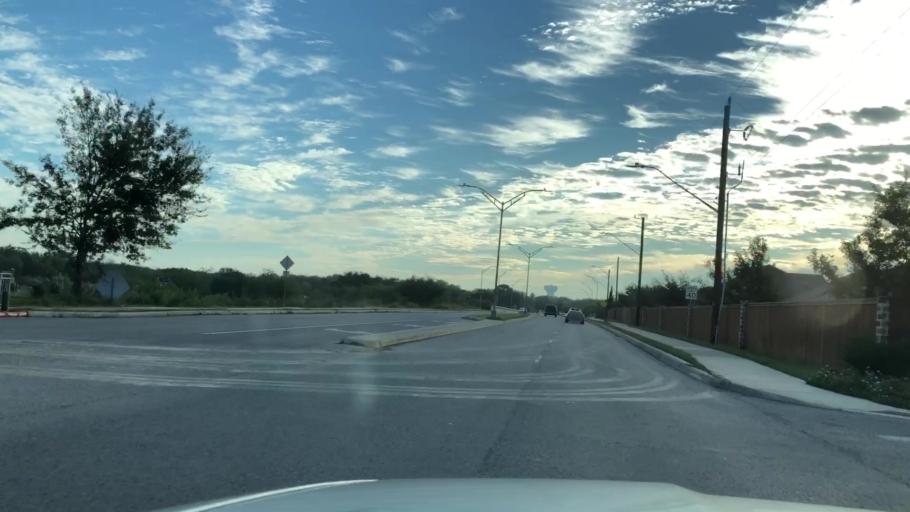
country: US
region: Texas
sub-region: Bexar County
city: Leon Valley
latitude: 29.5415
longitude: -98.6342
